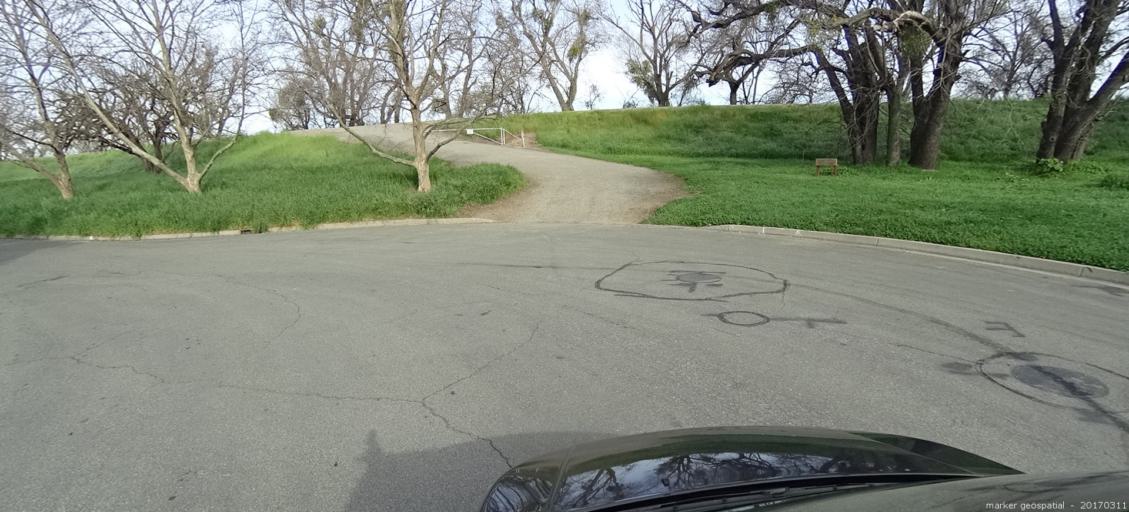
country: US
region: California
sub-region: Yolo County
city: West Sacramento
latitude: 38.5140
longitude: -121.5448
